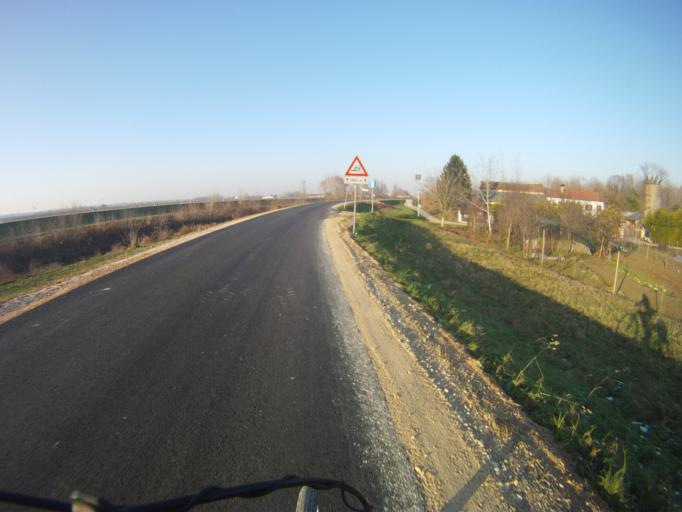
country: IT
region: Veneto
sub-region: Provincia di Padova
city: Legnaro
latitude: 45.3351
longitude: 11.9370
